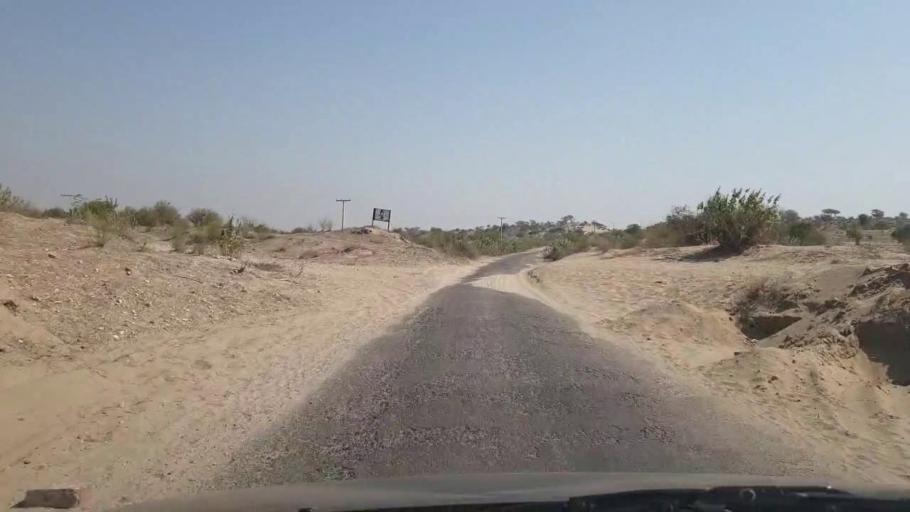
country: PK
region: Sindh
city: Chor
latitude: 25.5937
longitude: 69.9525
